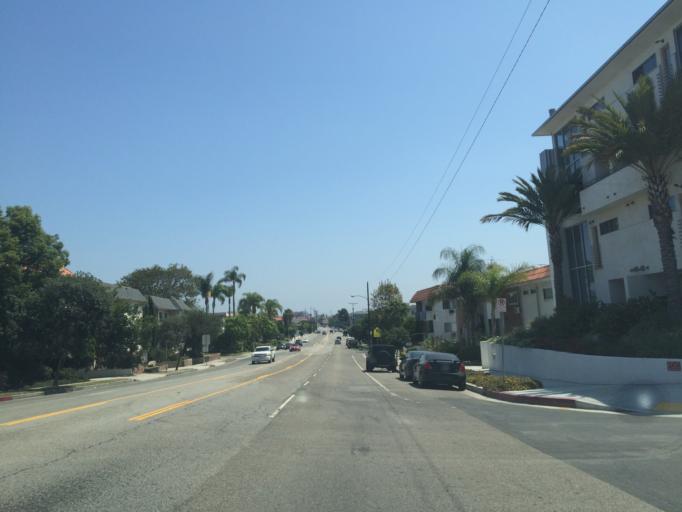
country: US
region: California
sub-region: Los Angeles County
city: Culver City
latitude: 34.0211
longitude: -118.4184
